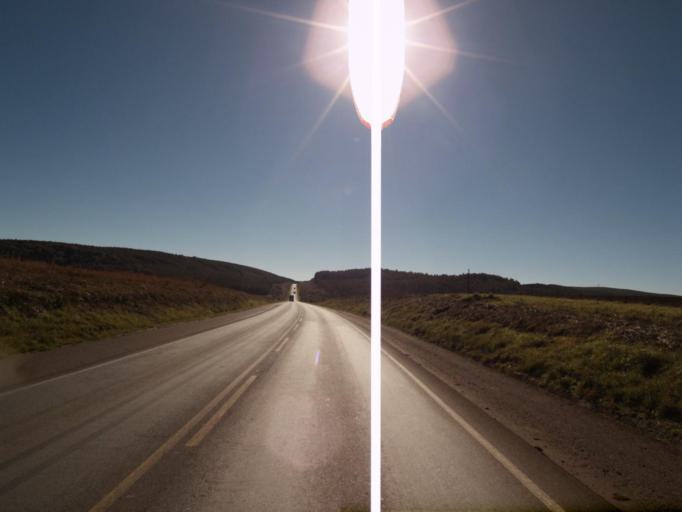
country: BR
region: Parana
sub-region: Palmas
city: Palmas
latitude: -26.6760
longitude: -51.5521
